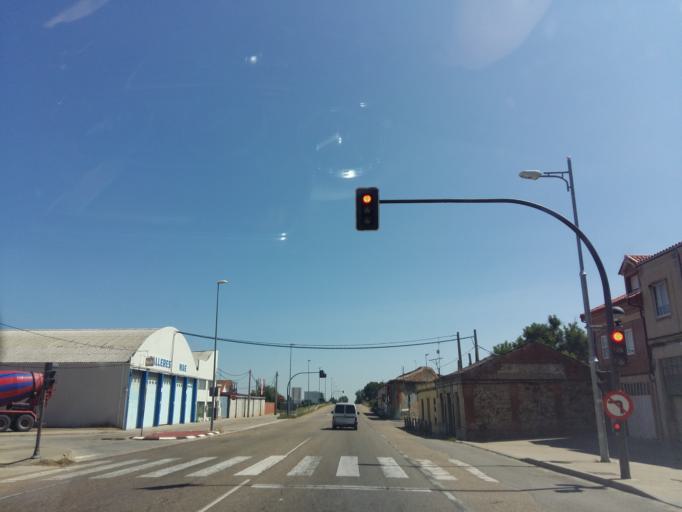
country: ES
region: Castille and Leon
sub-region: Provincia de Leon
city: Astorga
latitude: 42.4510
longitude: -6.0537
